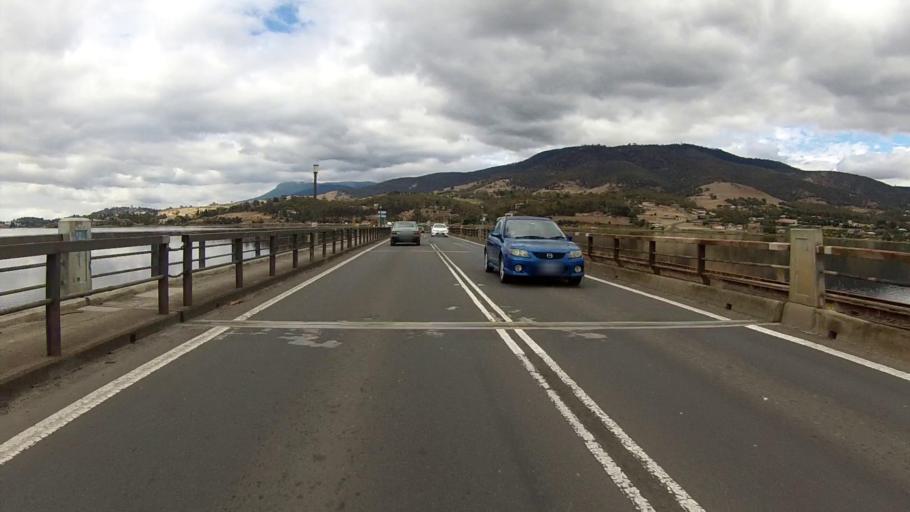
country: AU
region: Tasmania
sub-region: Brighton
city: Bridgewater
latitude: -42.7419
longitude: 147.2254
